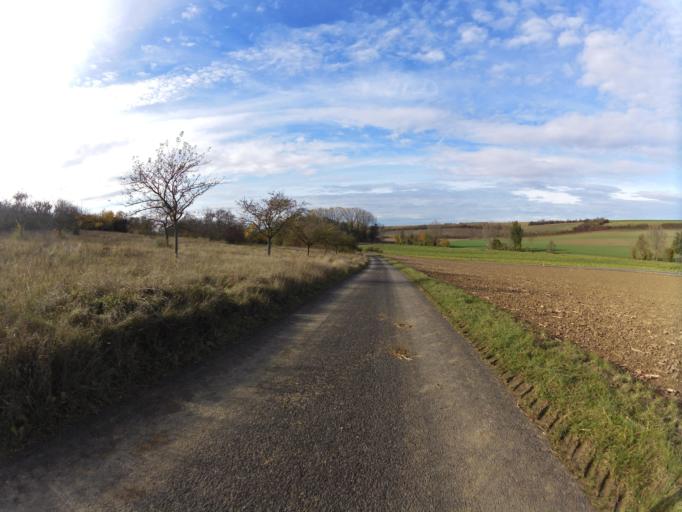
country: DE
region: Bavaria
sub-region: Regierungsbezirk Unterfranken
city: Giebelstadt
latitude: 49.6703
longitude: 9.9782
